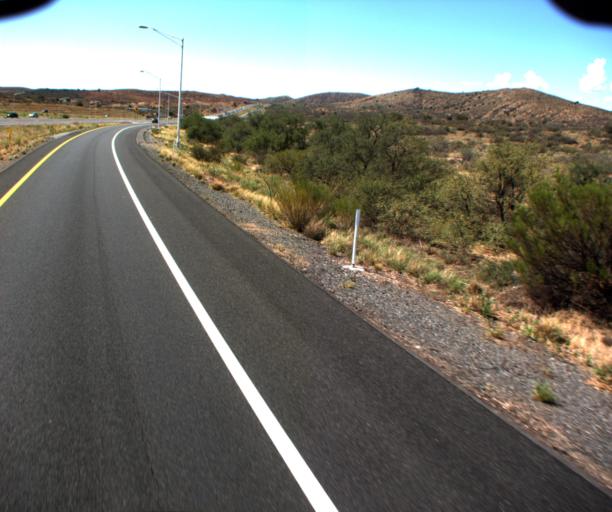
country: US
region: Arizona
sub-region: Yavapai County
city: Cordes Lakes
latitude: 34.3272
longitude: -112.1222
